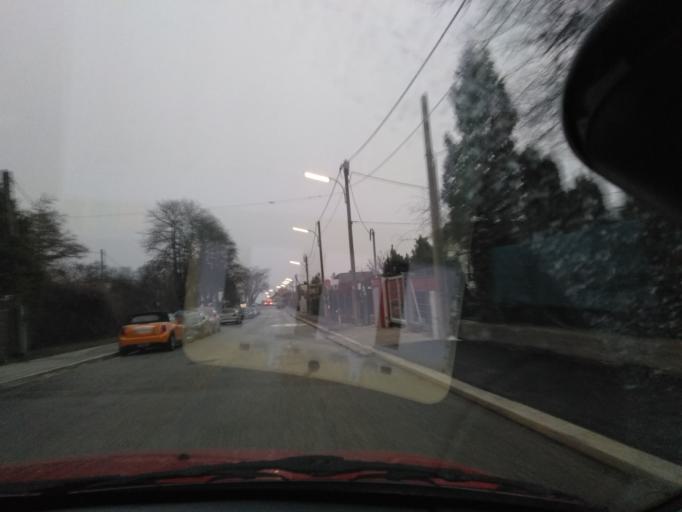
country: AT
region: Vienna
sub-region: Wien Stadt
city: Vienna
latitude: 48.2313
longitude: 16.3095
